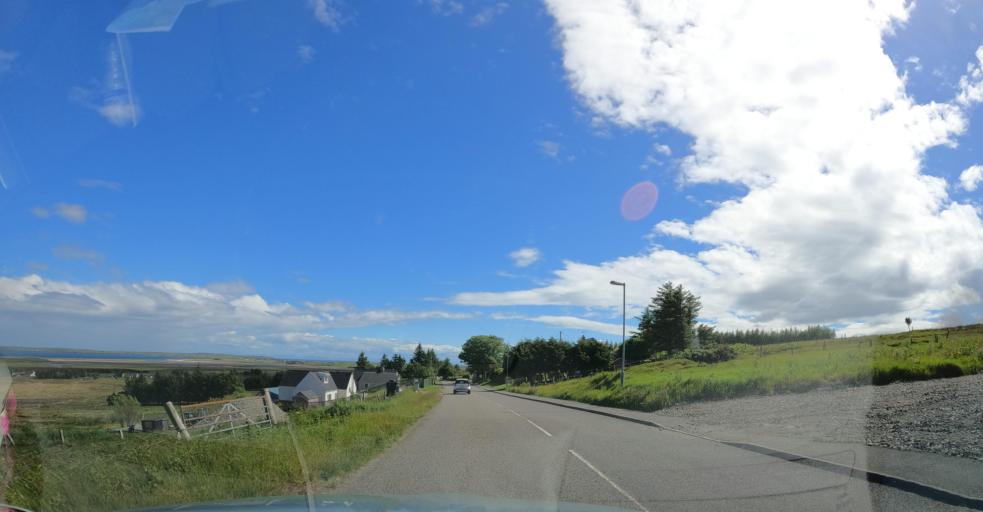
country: GB
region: Scotland
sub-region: Eilean Siar
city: Isle of Lewis
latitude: 58.2410
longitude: -6.3897
